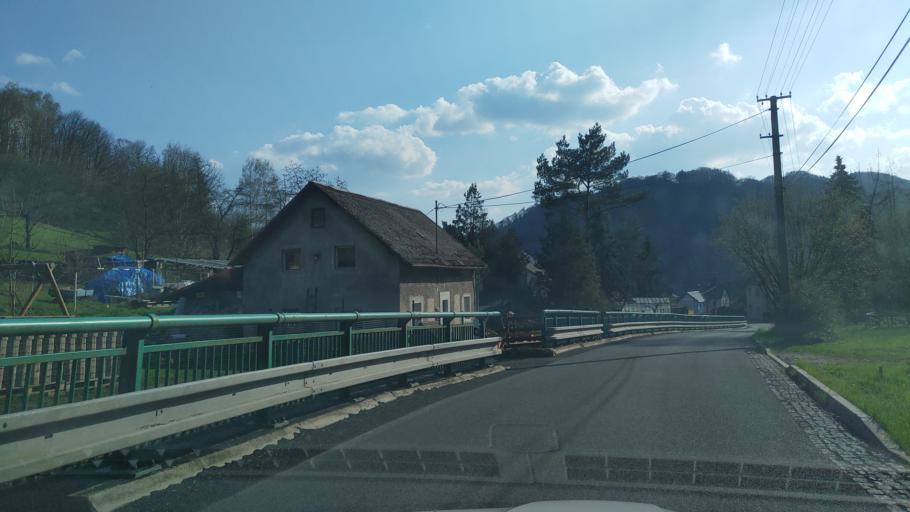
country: CZ
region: Ustecky
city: Povrly
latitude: 50.7056
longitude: 14.2059
